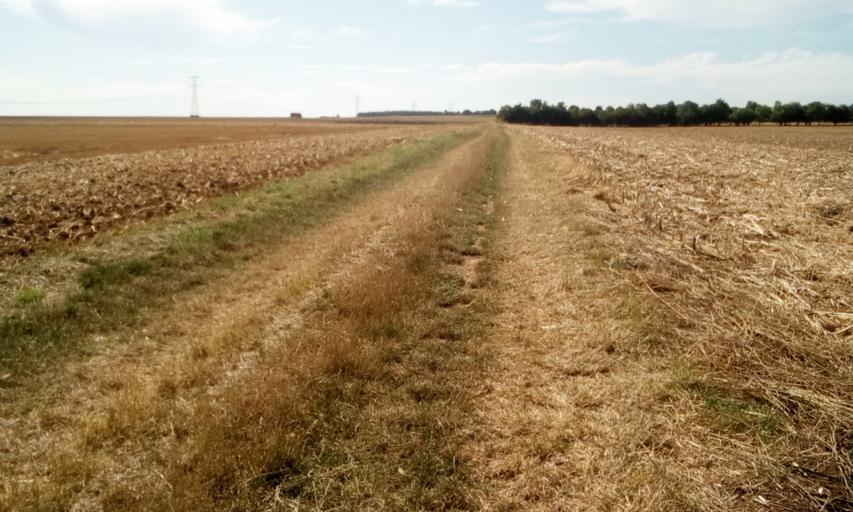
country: FR
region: Lower Normandy
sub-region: Departement du Calvados
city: Eterville
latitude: 49.1240
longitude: -0.4289
